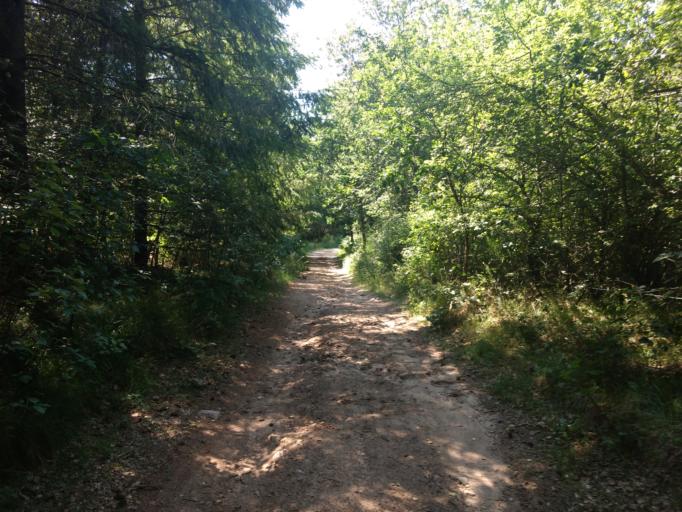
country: FR
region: Midi-Pyrenees
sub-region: Departement de l'Aveyron
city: La Loubiere
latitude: 44.3705
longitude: 2.7412
